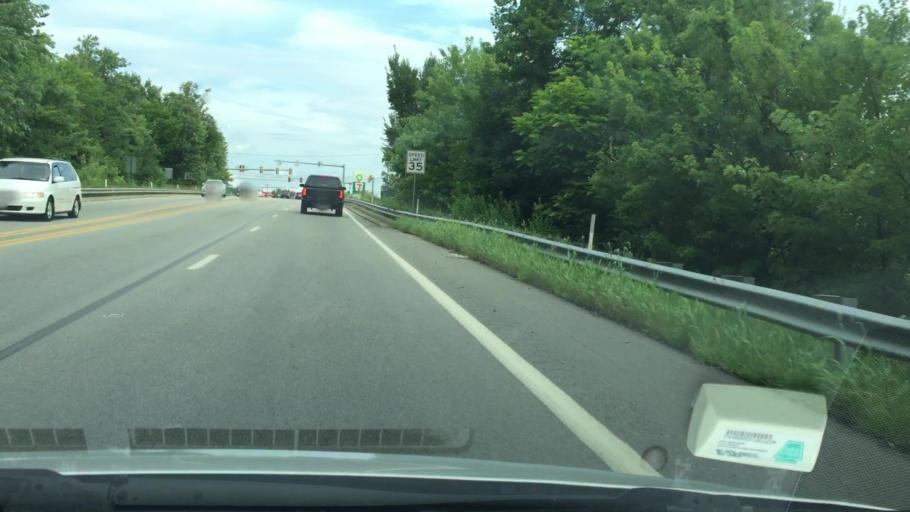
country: US
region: Pennsylvania
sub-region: Westmoreland County
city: Arnold
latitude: 40.5852
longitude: -79.7485
